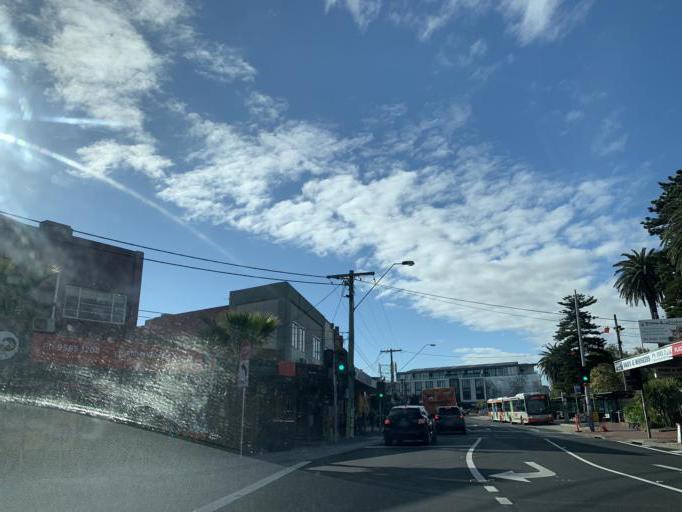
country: AU
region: Victoria
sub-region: Kingston
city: Mentone
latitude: -37.9826
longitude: 145.0650
